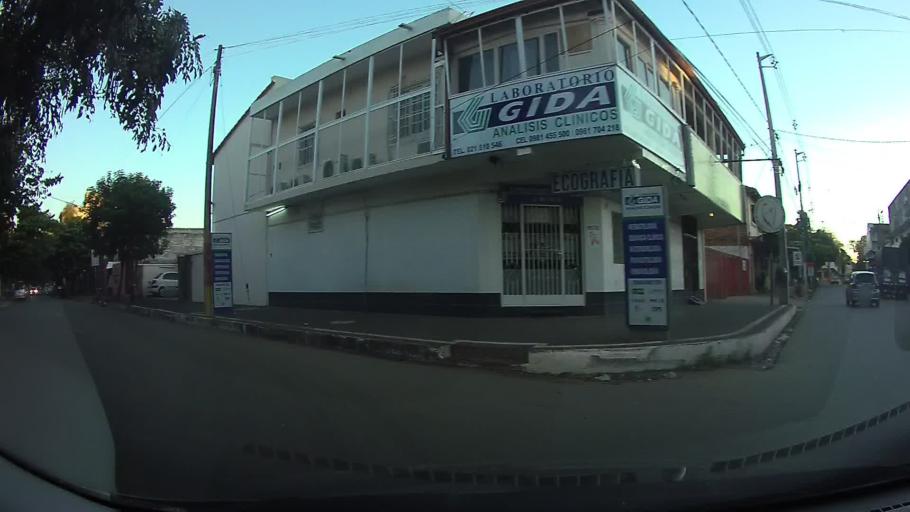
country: PY
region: Central
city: Fernando de la Mora
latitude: -25.3219
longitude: -57.5545
